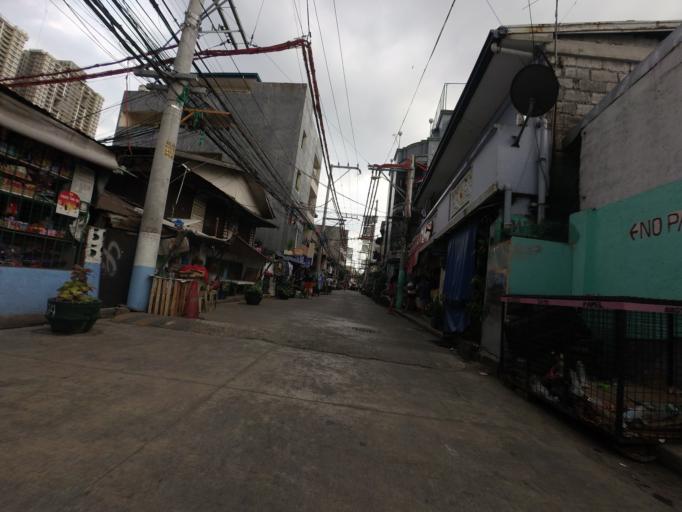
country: PH
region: Metro Manila
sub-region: City of Manila
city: Port Area
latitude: 14.5572
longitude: 120.9936
